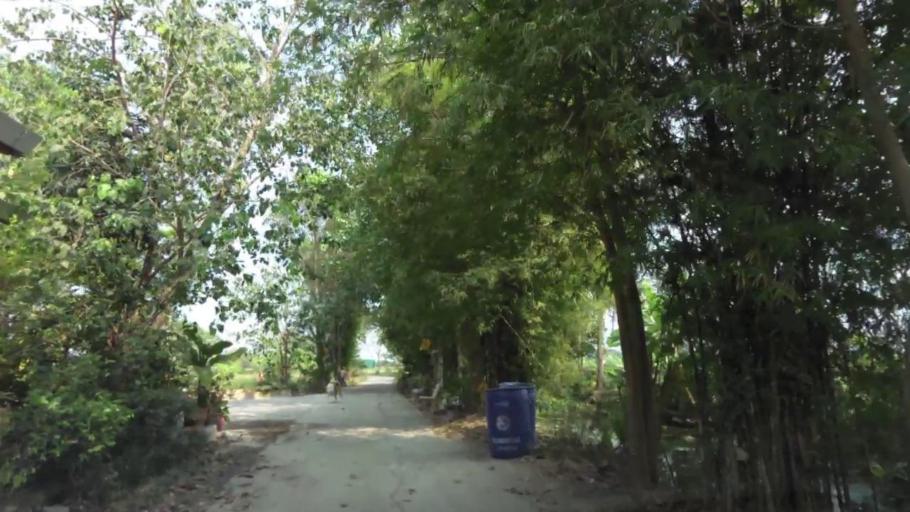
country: TH
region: Phra Nakhon Si Ayutthaya
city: Phra Nakhon Si Ayutthaya
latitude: 14.3145
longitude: 100.5578
